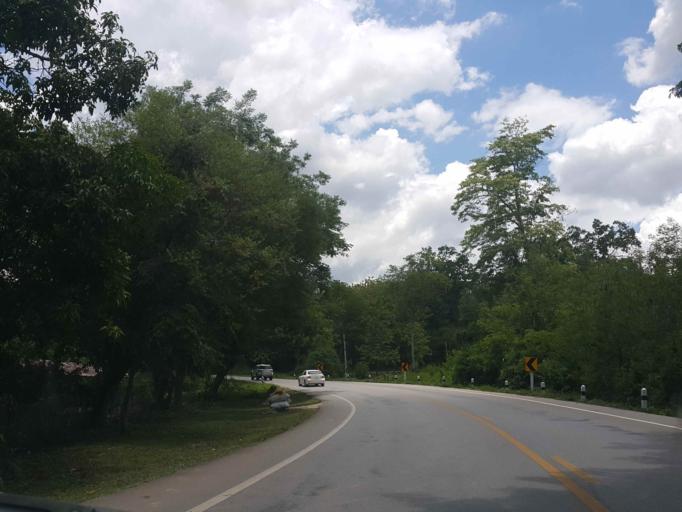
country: TH
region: Nan
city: Wiang Sa
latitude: 18.5172
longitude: 100.5956
